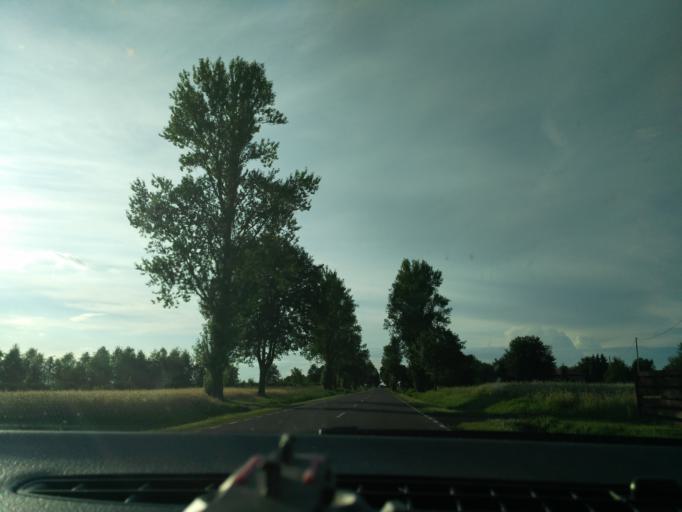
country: PL
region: Lublin Voivodeship
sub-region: Powiat krasnicki
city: Krasnik
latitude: 50.8745
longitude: 22.2677
